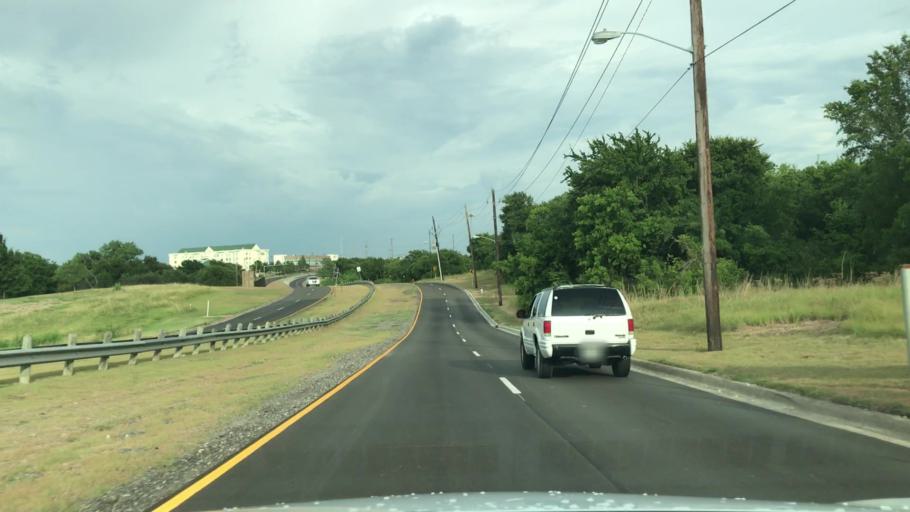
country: US
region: Texas
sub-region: Dallas County
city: Sunnyvale
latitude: 32.8365
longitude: -96.6186
